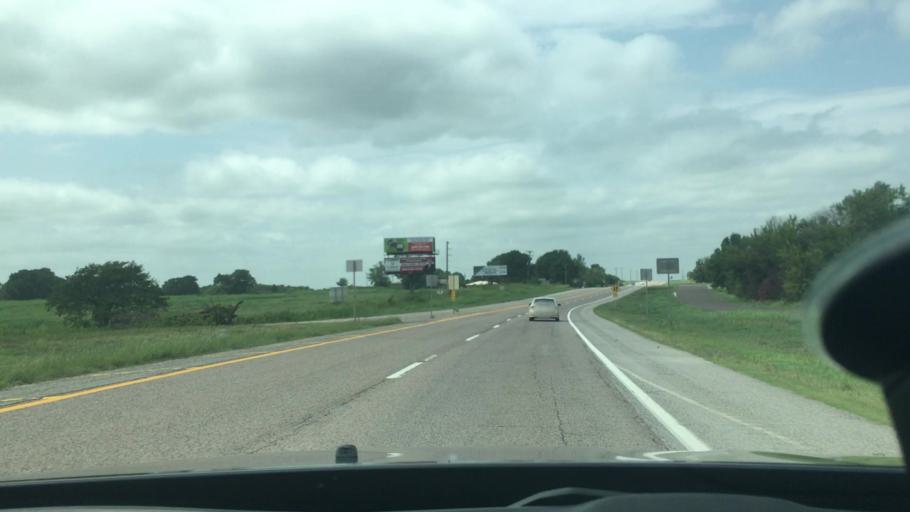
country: US
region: Oklahoma
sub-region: Pontotoc County
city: Ada
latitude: 34.7869
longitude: -96.7261
